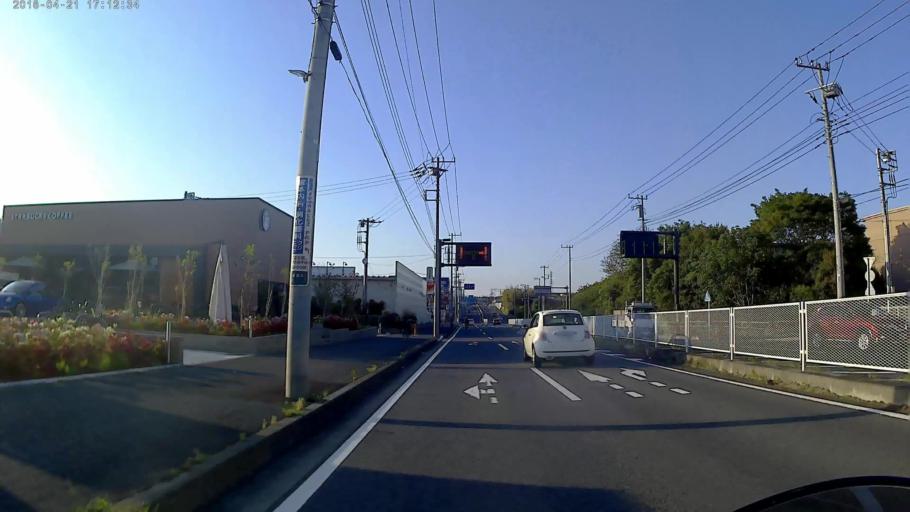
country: JP
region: Kanagawa
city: Fujisawa
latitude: 35.4011
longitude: 139.4419
